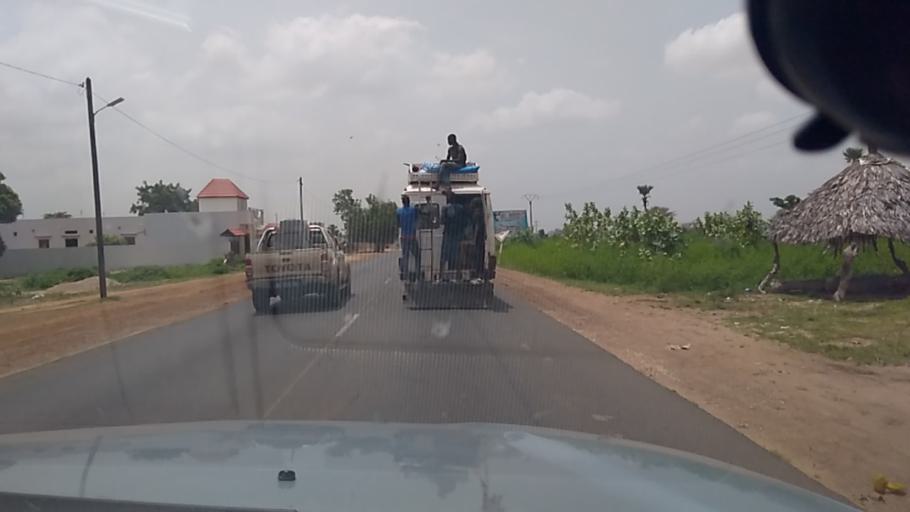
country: SN
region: Thies
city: Mekhe
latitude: 15.0197
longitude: -16.7359
